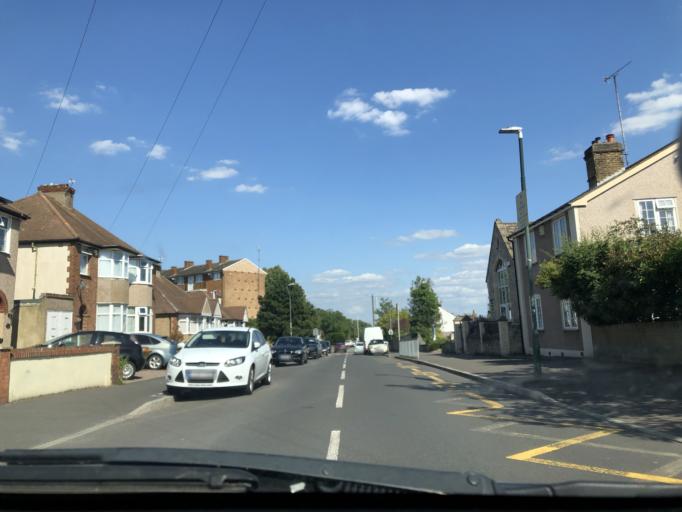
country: GB
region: England
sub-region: Greater London
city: Bexley
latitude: 51.4543
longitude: 0.1719
